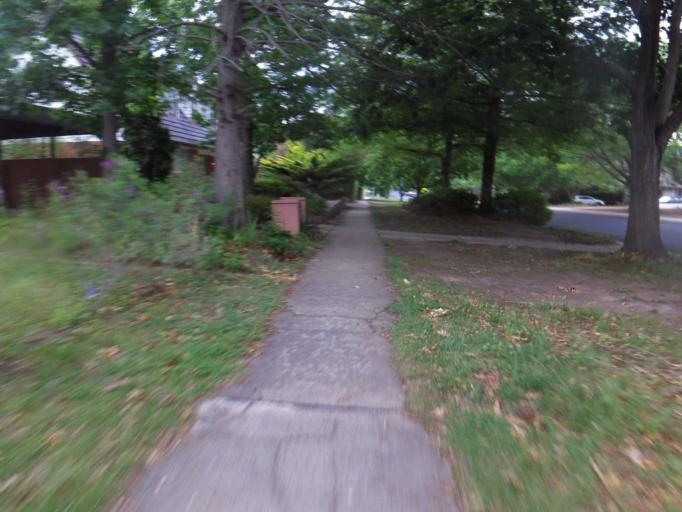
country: AU
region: Australian Capital Territory
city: Forrest
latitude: -35.3403
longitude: 149.1282
